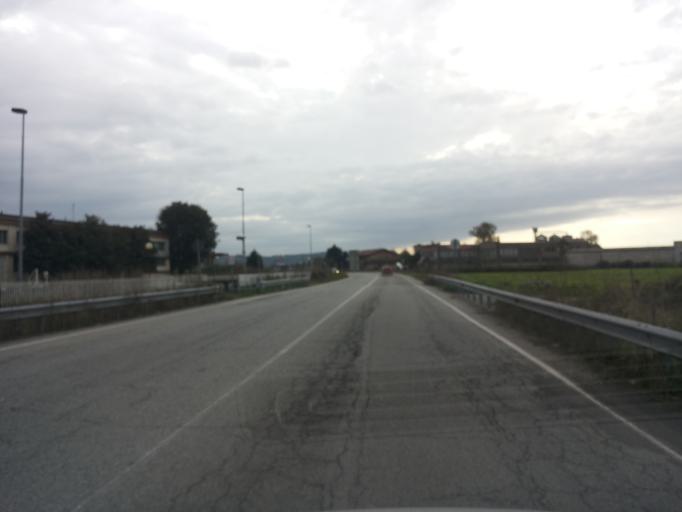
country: IT
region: Piedmont
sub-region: Provincia di Alessandria
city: Villanova Monferrato
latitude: 45.1674
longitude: 8.4638
